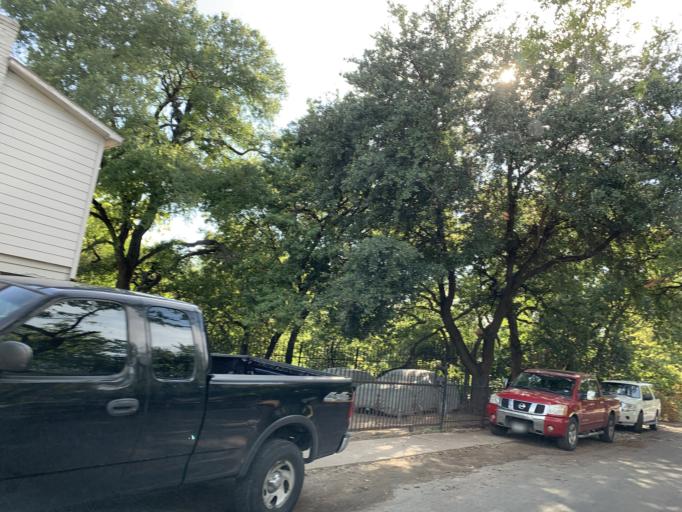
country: US
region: Texas
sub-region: Dallas County
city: Dallas
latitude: 32.7350
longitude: -96.8322
